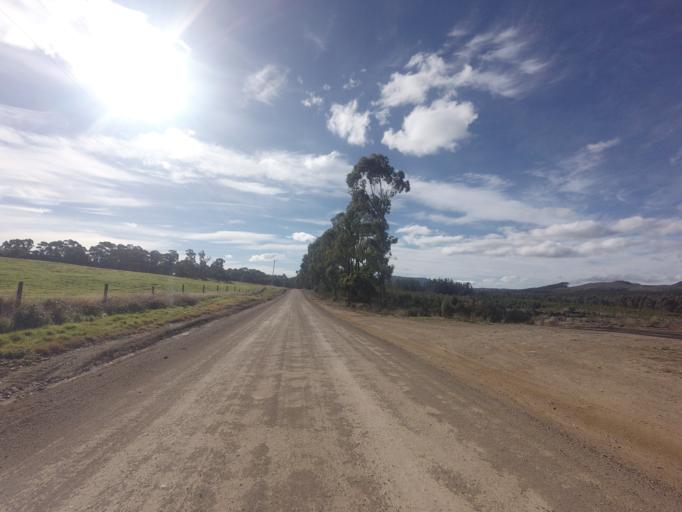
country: AU
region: Tasmania
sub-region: Clarence
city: Sandford
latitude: -43.1667
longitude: 147.7681
